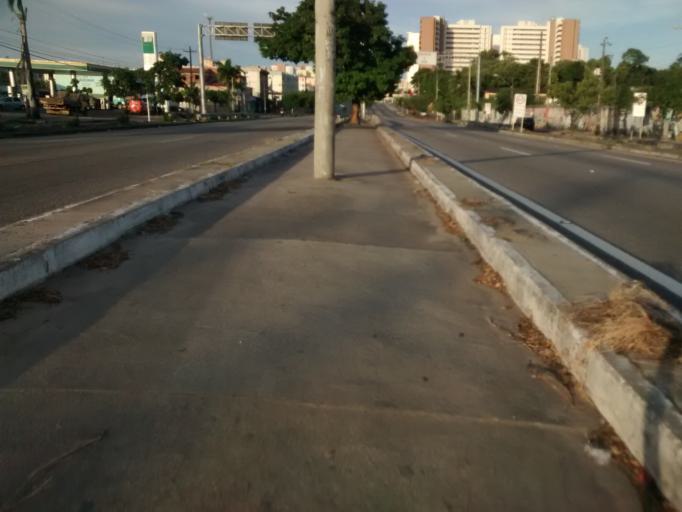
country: BR
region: Ceara
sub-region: Fortaleza
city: Fortaleza
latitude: -3.7373
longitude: -38.5744
